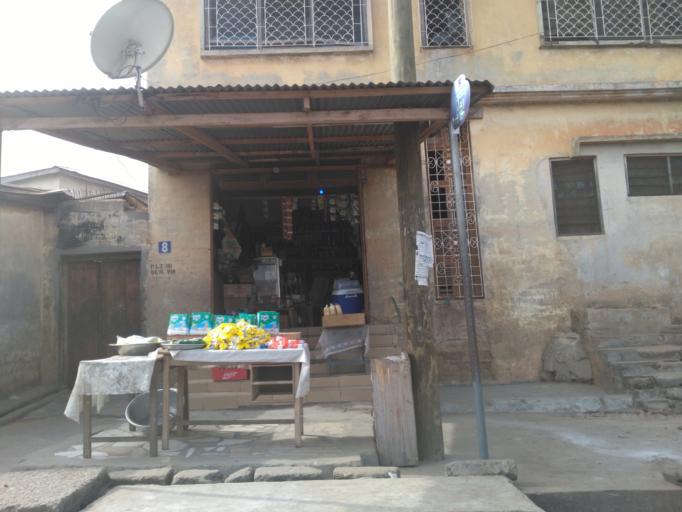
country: GH
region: Ashanti
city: Kumasi
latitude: 6.6962
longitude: -1.6131
